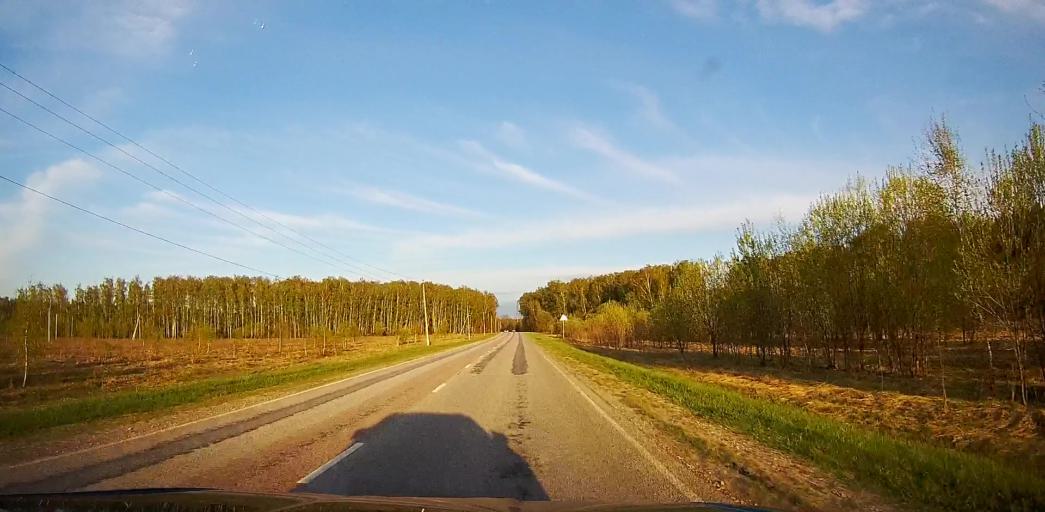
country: RU
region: Moskovskaya
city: Meshcherino
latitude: 55.2291
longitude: 38.3809
